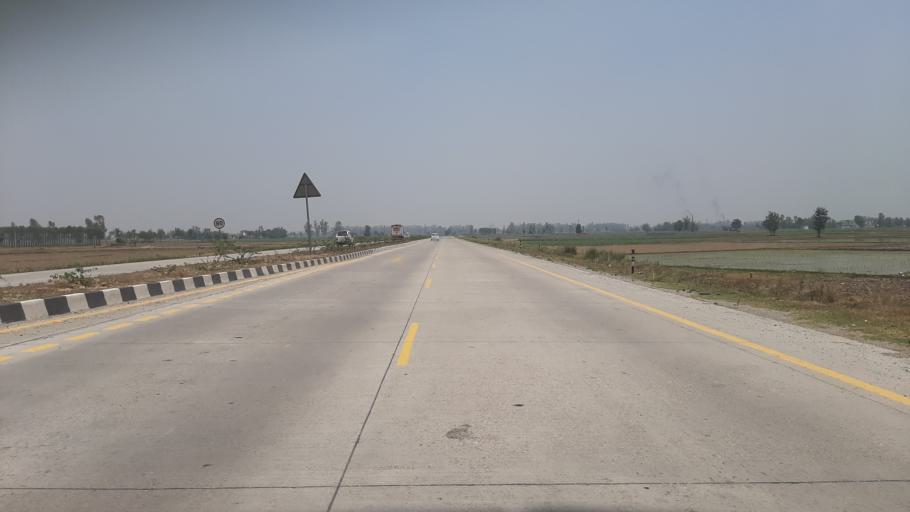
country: IN
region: Haryana
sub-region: Yamunanagar
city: Yamunanagar
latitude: 30.1716
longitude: 77.2273
